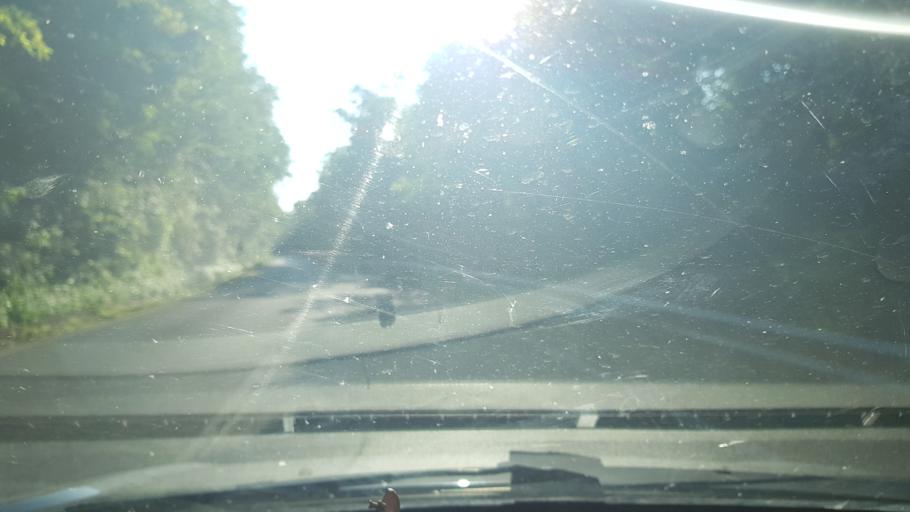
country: IT
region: Friuli Venezia Giulia
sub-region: Provincia di Gorizia
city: Farra d'Isonzo
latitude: 45.8968
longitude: 13.5444
